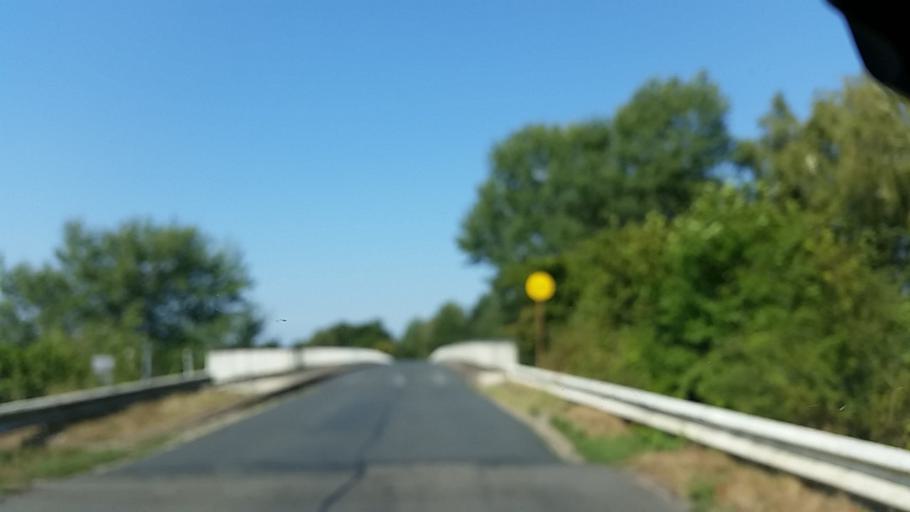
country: DE
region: Lower Saxony
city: Schoneworde
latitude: 52.5986
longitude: 10.6806
